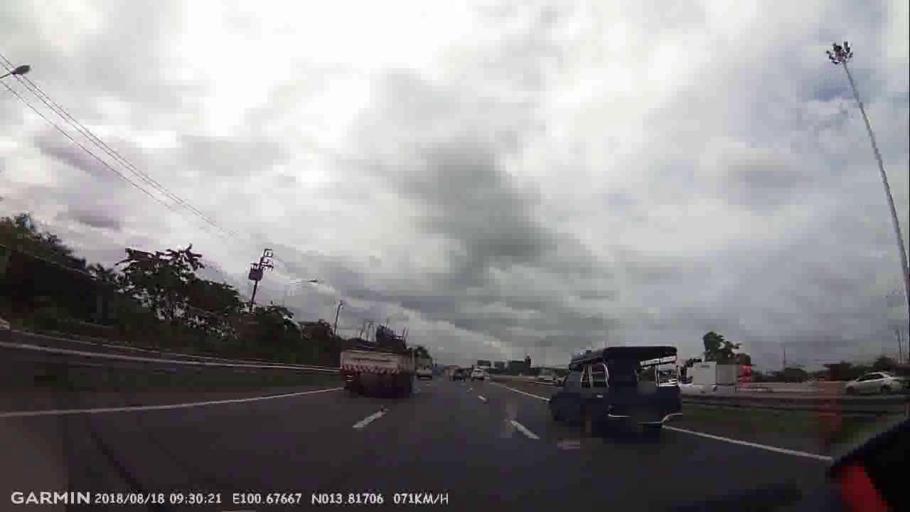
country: TH
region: Bangkok
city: Khan Na Yao
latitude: 13.8168
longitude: 100.6768
